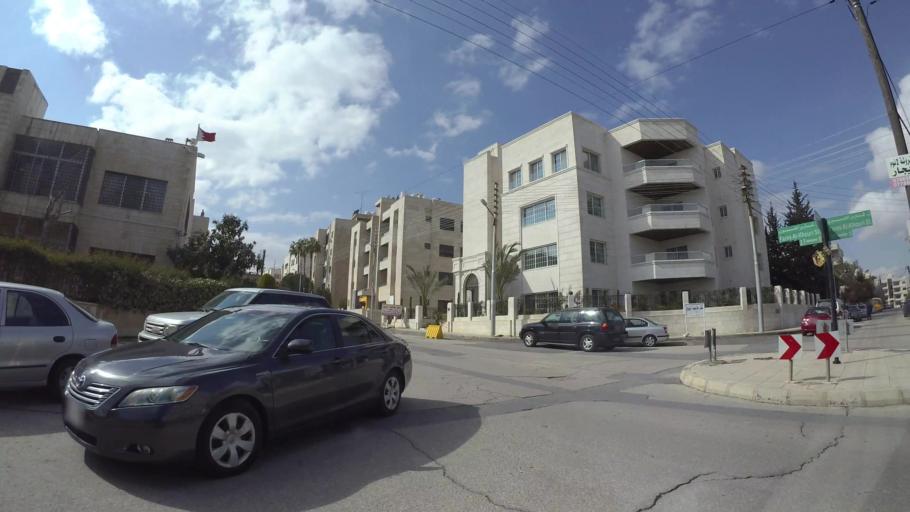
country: JO
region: Amman
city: Amman
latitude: 31.9725
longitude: 35.8949
